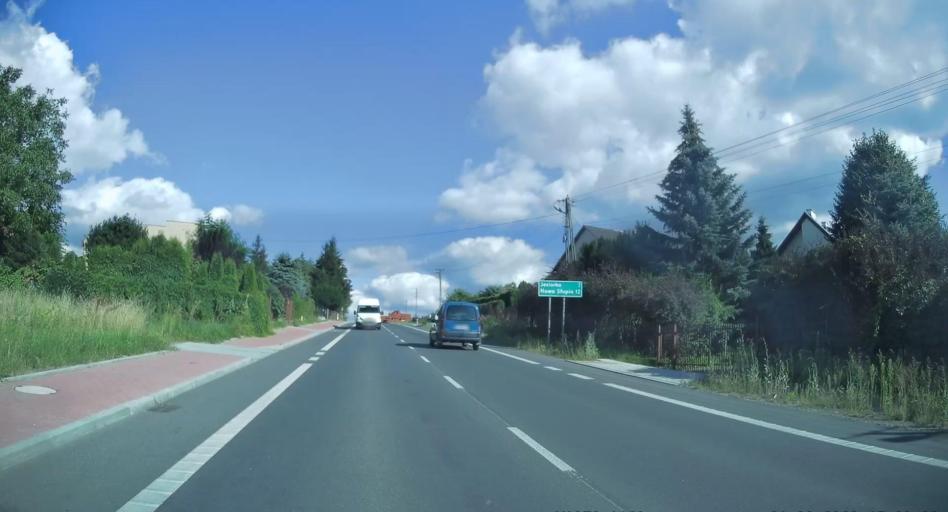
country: PL
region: Swietokrzyskie
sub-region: Powiat kielecki
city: Bodzentyn
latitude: 50.9376
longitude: 20.9536
